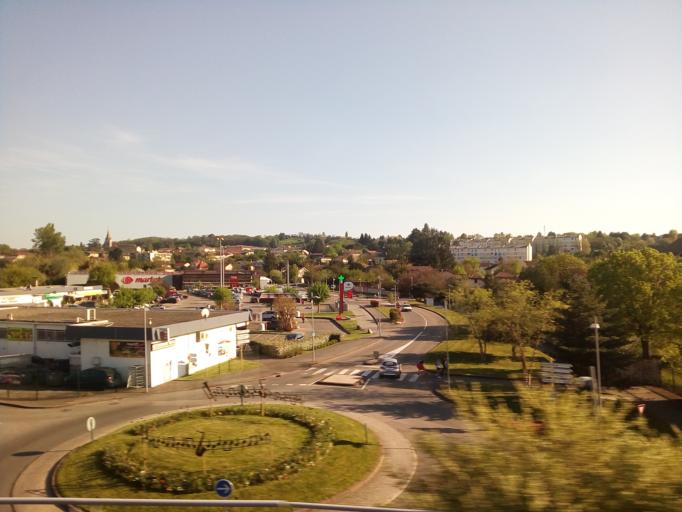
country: FR
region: Rhone-Alpes
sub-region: Departement de l'Isere
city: Saint-Quentin-Fallavier
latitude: 45.6377
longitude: 5.1082
